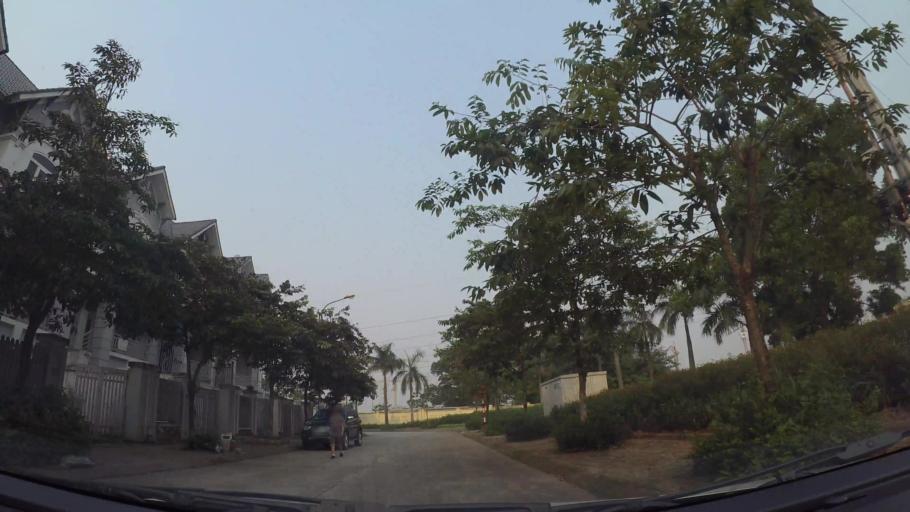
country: VN
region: Ha Noi
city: Cau Dien
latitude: 21.0047
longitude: 105.7338
